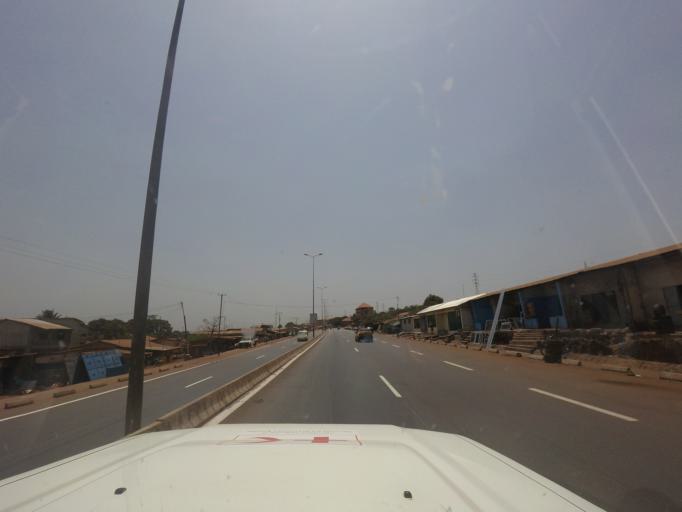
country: GN
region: Kindia
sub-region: Prefecture de Dubreka
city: Dubreka
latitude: 9.6905
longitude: -13.5103
